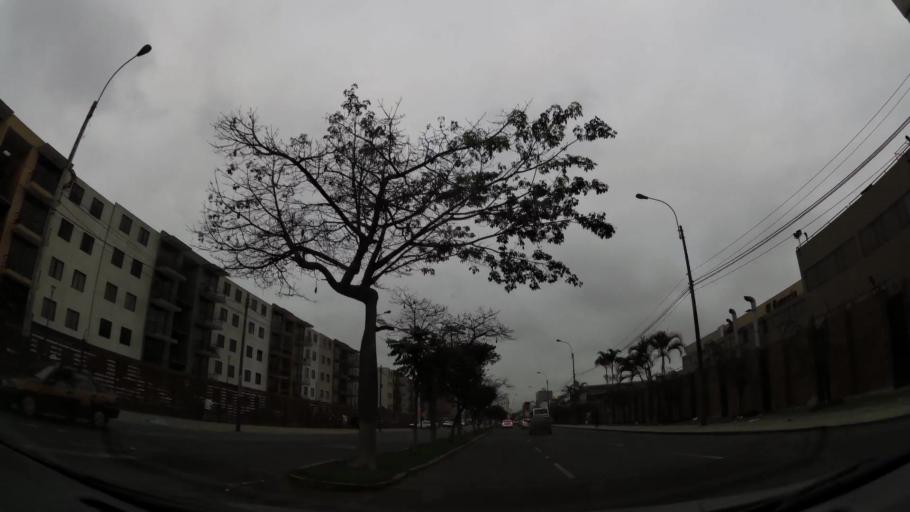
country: PE
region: Callao
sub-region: Callao
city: Callao
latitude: -12.0705
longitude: -77.0754
